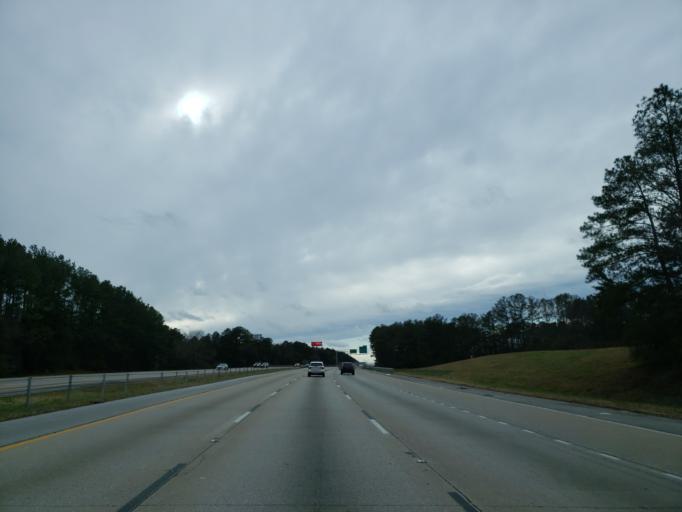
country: US
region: Alabama
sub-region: Jefferson County
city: Vestavia Hills
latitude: 33.4082
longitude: -86.7622
